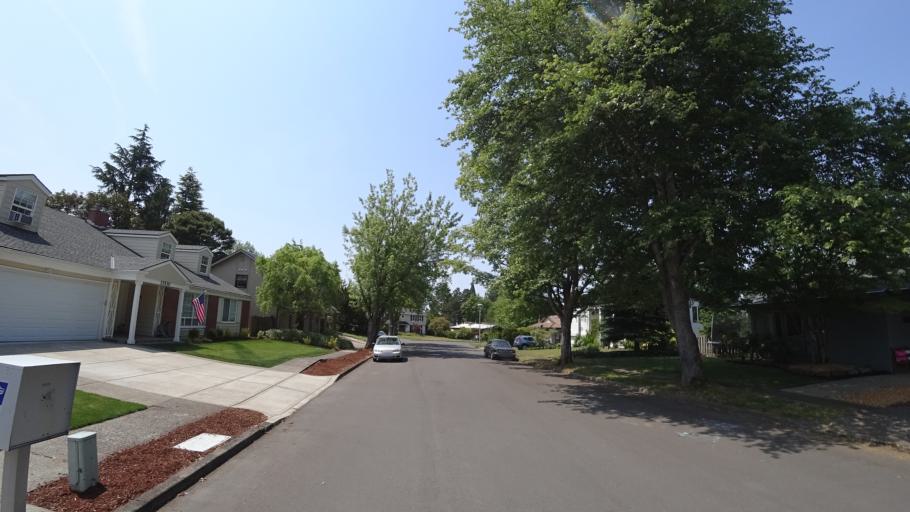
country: US
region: Oregon
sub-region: Washington County
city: Oak Hills
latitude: 45.5371
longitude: -122.8367
